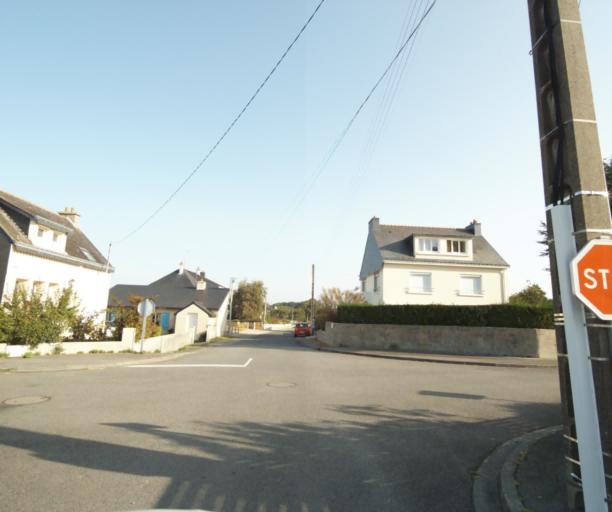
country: FR
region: Brittany
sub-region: Departement du Morbihan
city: Riantec
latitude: 47.7096
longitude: -3.3188
